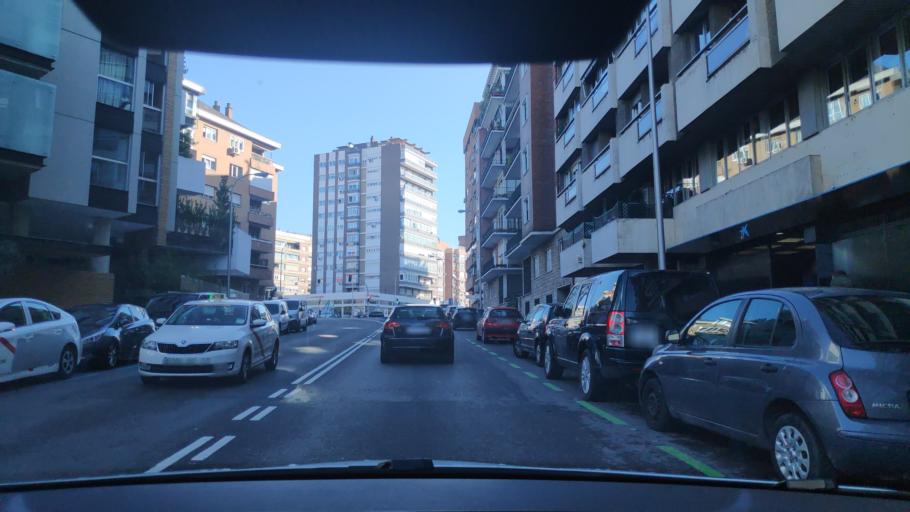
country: ES
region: Madrid
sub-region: Provincia de Madrid
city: Chamartin
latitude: 40.4557
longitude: -3.6817
